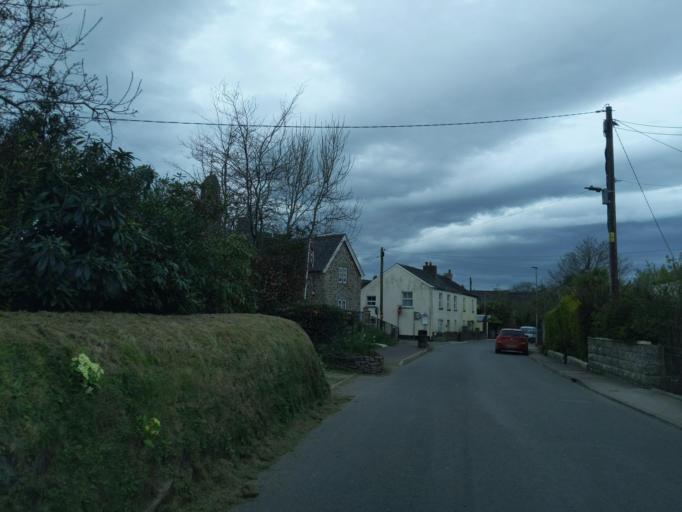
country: GB
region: England
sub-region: Devon
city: Great Torrington
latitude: 50.9159
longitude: -4.0586
